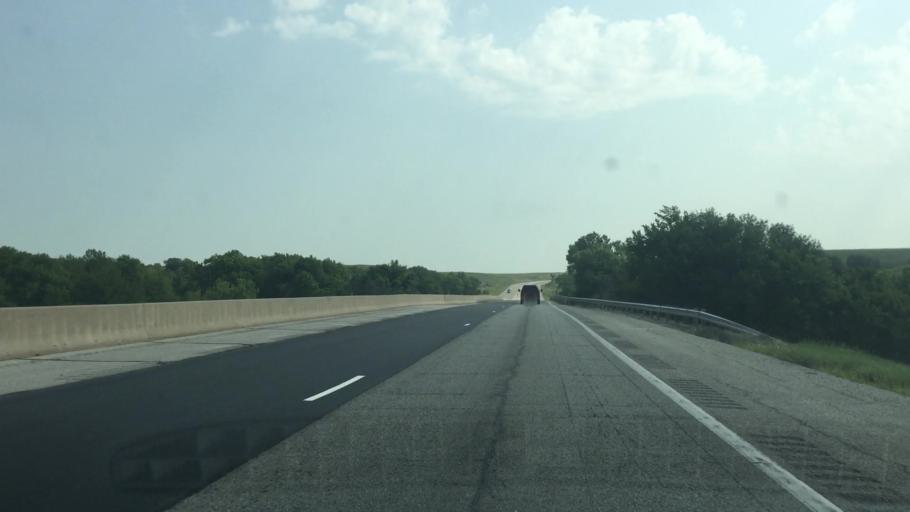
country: US
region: Kansas
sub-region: Chase County
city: Cottonwood Falls
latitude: 38.1273
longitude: -96.5489
